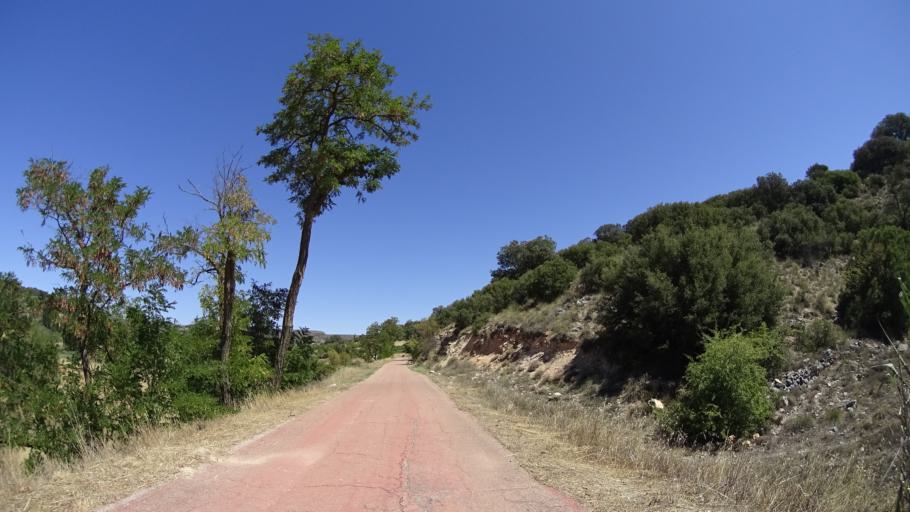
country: ES
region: Madrid
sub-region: Provincia de Madrid
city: Ambite
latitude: 40.3028
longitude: -3.1925
